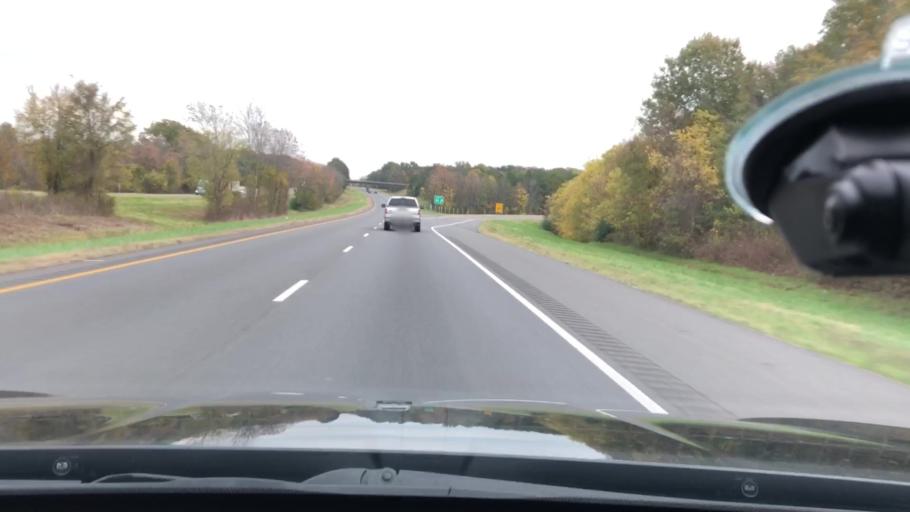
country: US
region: Arkansas
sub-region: Hempstead County
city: Hope
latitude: 33.7343
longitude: -93.5278
